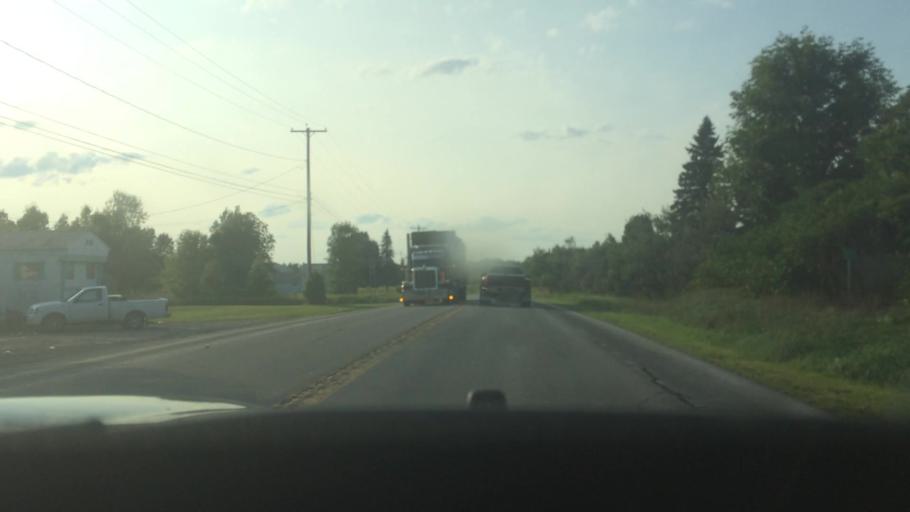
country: US
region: New York
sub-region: St. Lawrence County
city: Ogdensburg
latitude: 44.6787
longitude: -75.4403
